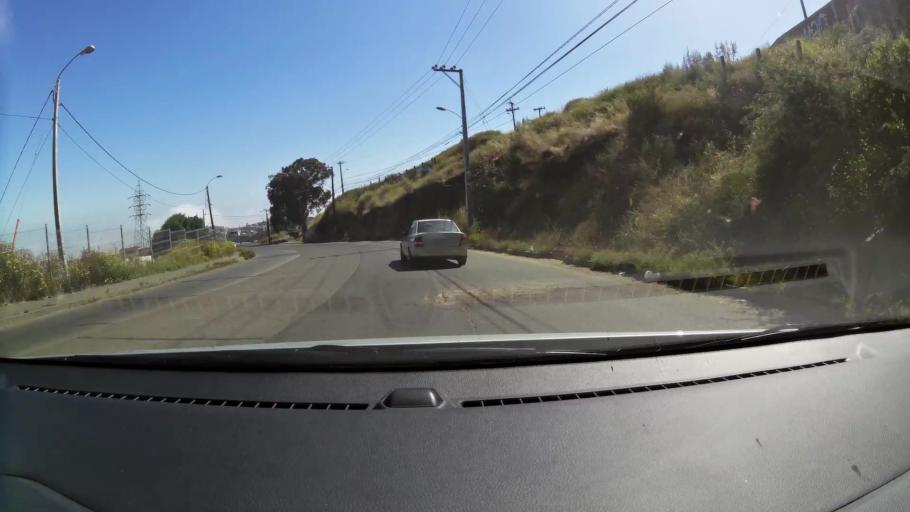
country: CL
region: Valparaiso
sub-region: Provincia de Valparaiso
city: Valparaiso
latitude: -33.0474
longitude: -71.6509
